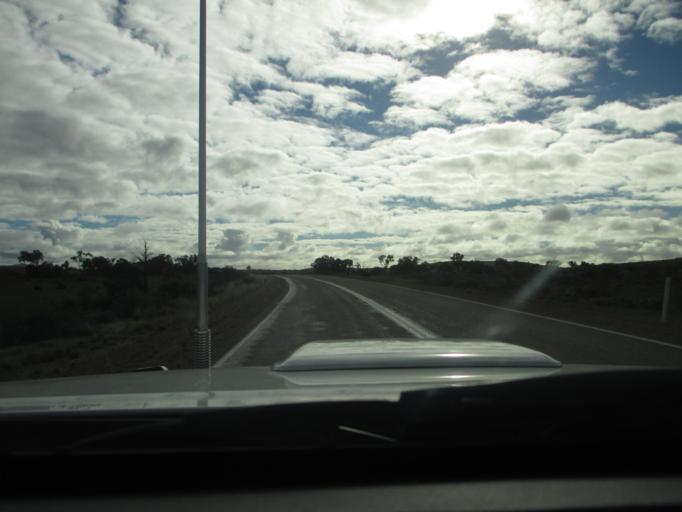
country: AU
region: South Australia
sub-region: Flinders Ranges
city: Quorn
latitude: -32.3133
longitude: 138.4851
